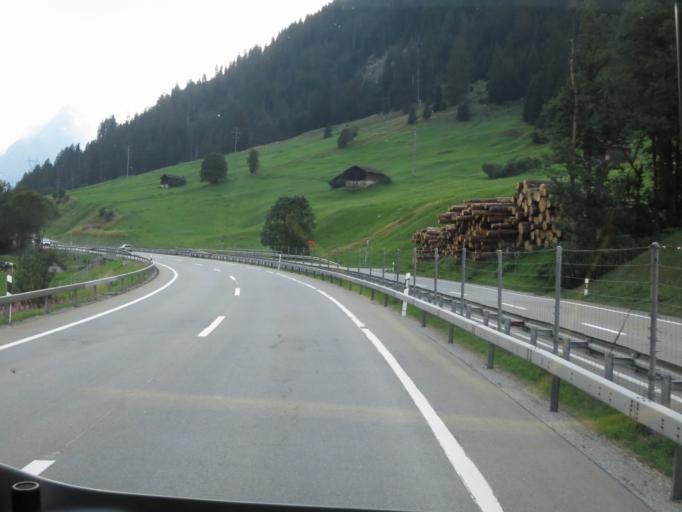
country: CH
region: Grisons
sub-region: Hinterrhein District
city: Hinterrhein
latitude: 46.5453
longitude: 9.2891
